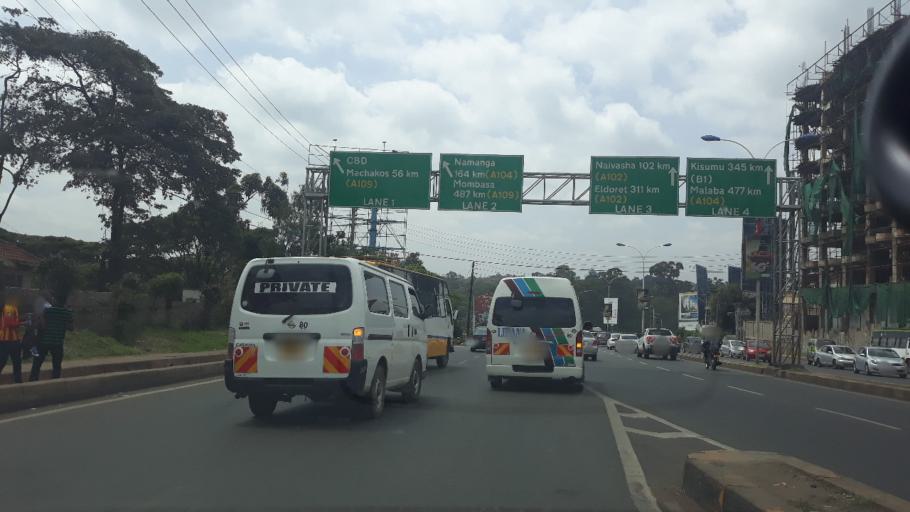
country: KE
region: Nairobi Area
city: Nairobi
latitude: -1.2731
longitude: 36.8141
